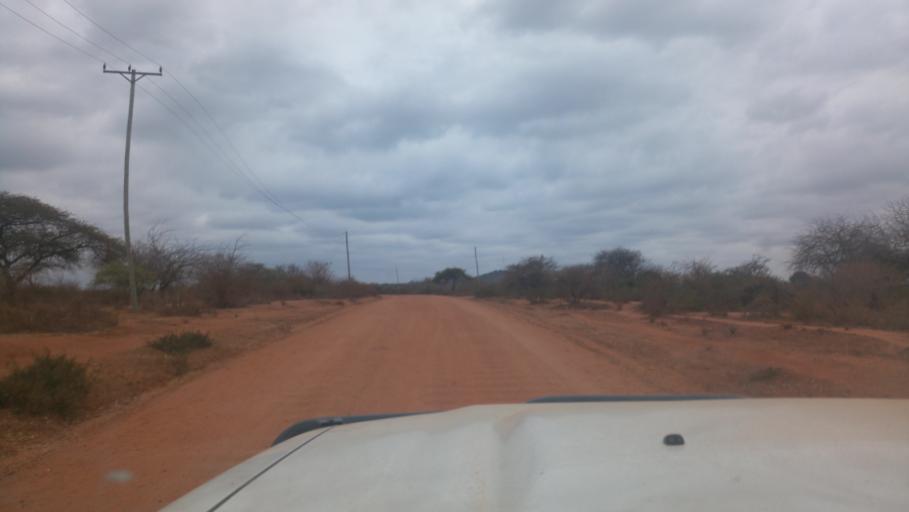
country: KE
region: Makueni
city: Wote
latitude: -1.9479
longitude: 38.0531
